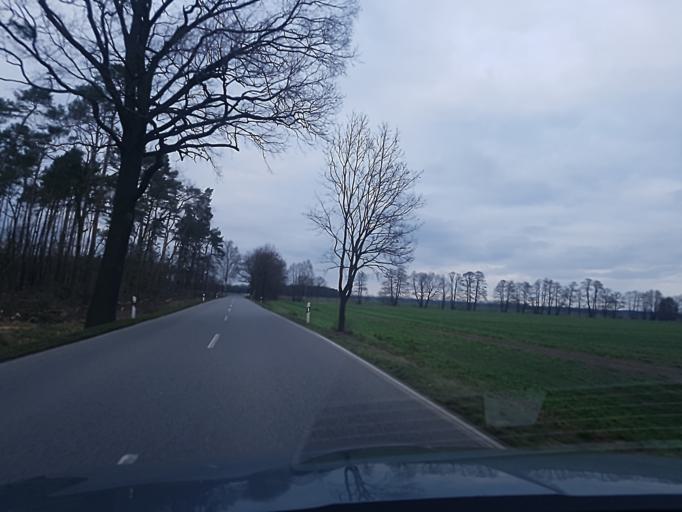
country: DE
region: Brandenburg
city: Finsterwalde
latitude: 51.6670
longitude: 13.6923
